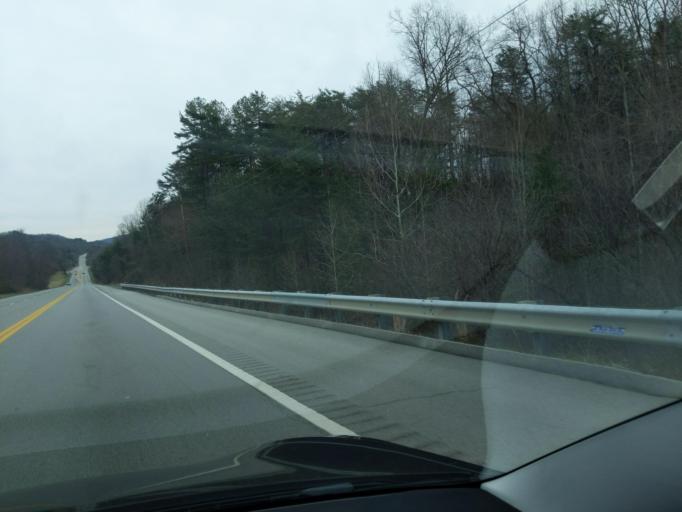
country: US
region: Kentucky
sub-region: Whitley County
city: Corbin
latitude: 36.9174
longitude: -84.0985
